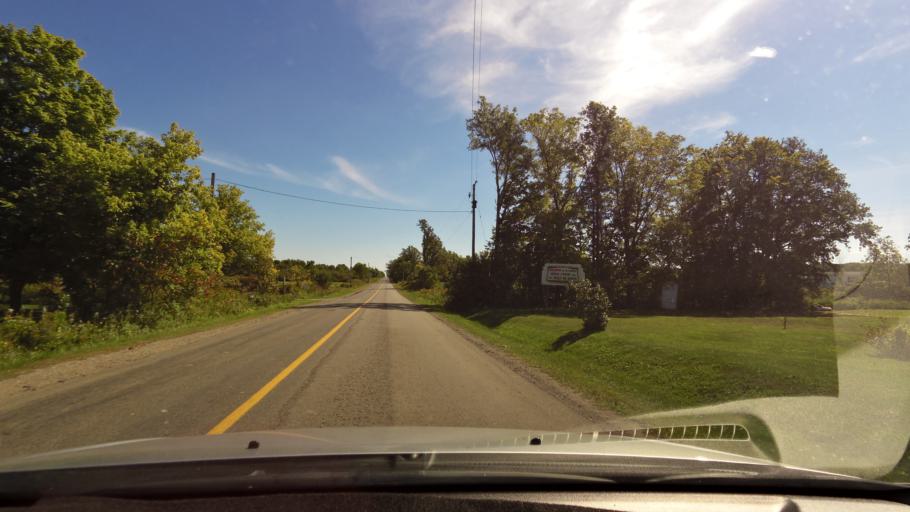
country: CA
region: Ontario
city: Ancaster
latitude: 43.0723
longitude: -80.0715
